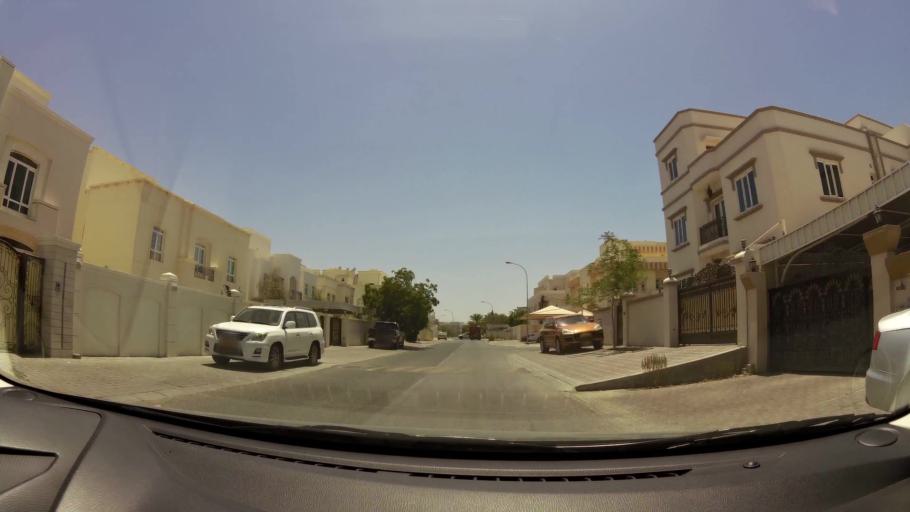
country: OM
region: Muhafazat Masqat
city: As Sib al Jadidah
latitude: 23.6149
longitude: 58.2274
